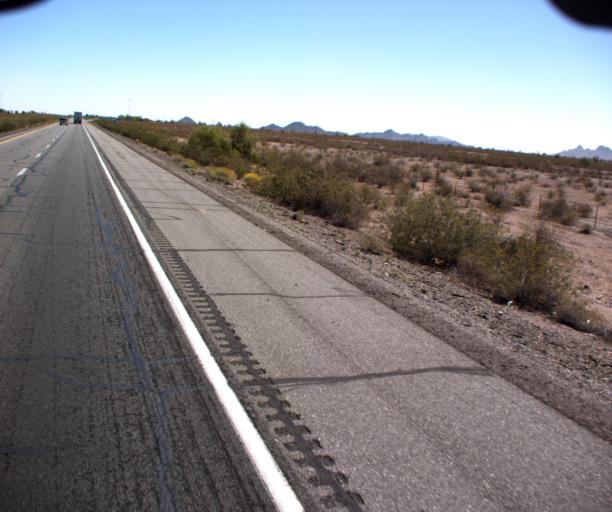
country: US
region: Arizona
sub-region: Maricopa County
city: Buckeye
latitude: 33.5220
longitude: -113.0798
